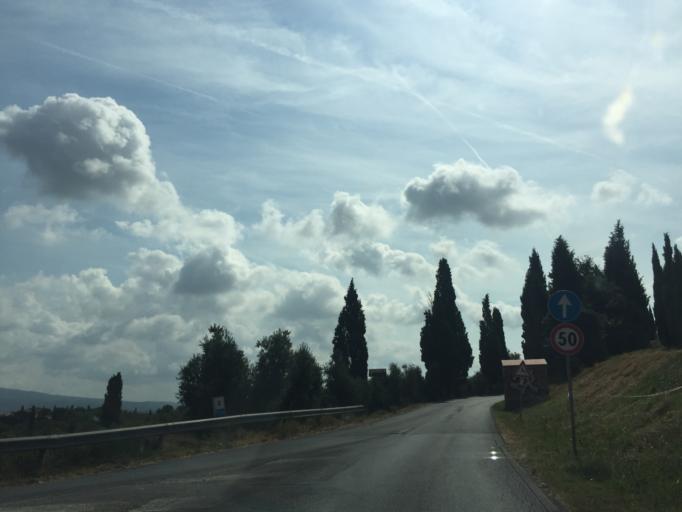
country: IT
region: Tuscany
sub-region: Province of Florence
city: Cerreto Guidi
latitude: 43.7524
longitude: 10.8825
